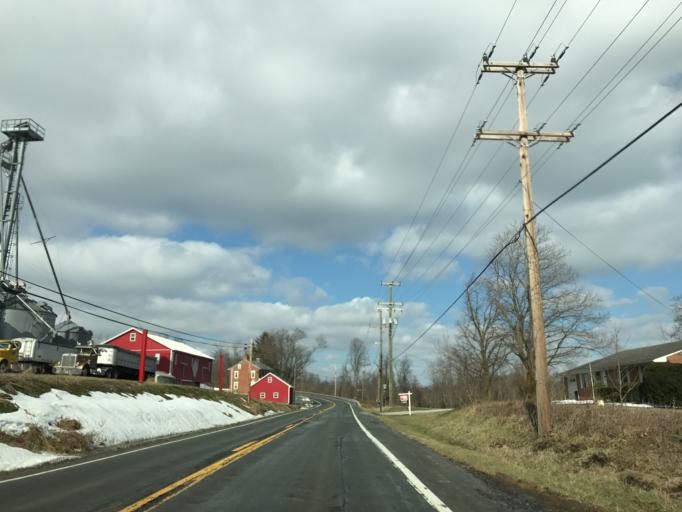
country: US
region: Maryland
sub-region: Carroll County
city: Manchester
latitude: 39.6839
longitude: -76.9208
